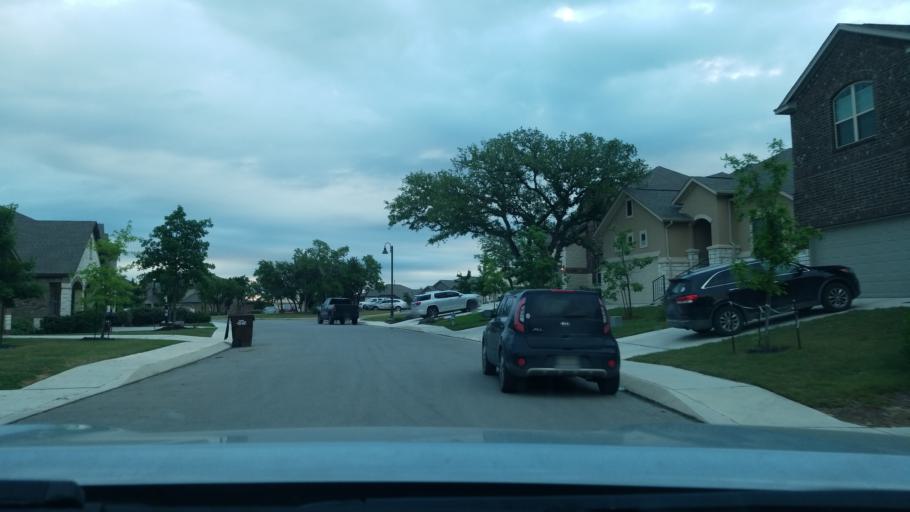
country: US
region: Texas
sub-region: Bexar County
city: Timberwood Park
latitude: 29.7161
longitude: -98.4562
